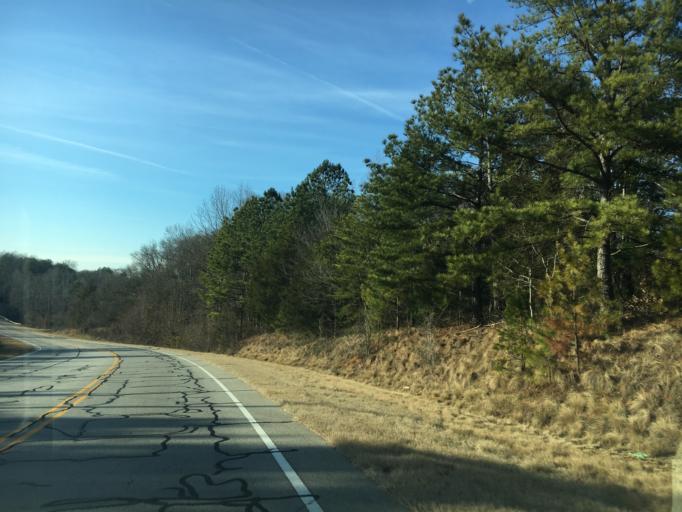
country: US
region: Georgia
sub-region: Franklin County
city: Lavonia
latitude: 34.4521
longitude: -83.0388
